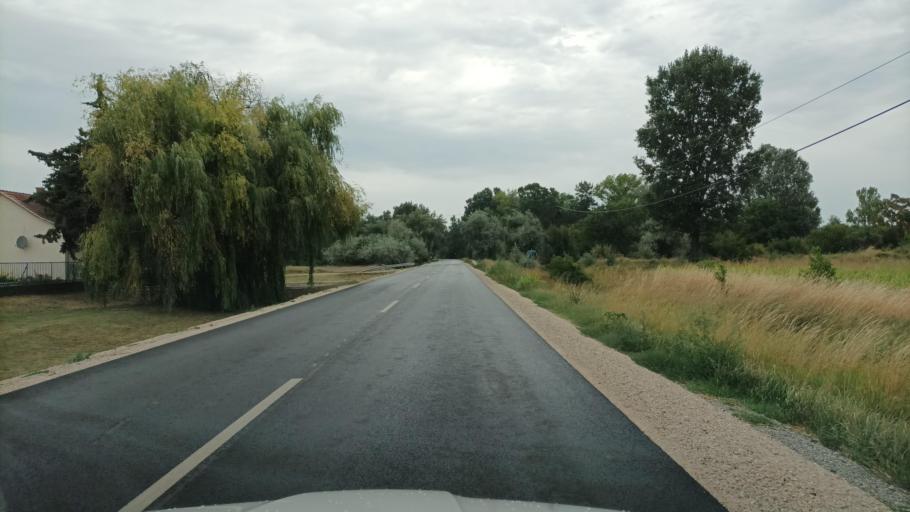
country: HU
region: Pest
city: Dabas
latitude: 47.2059
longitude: 19.2694
